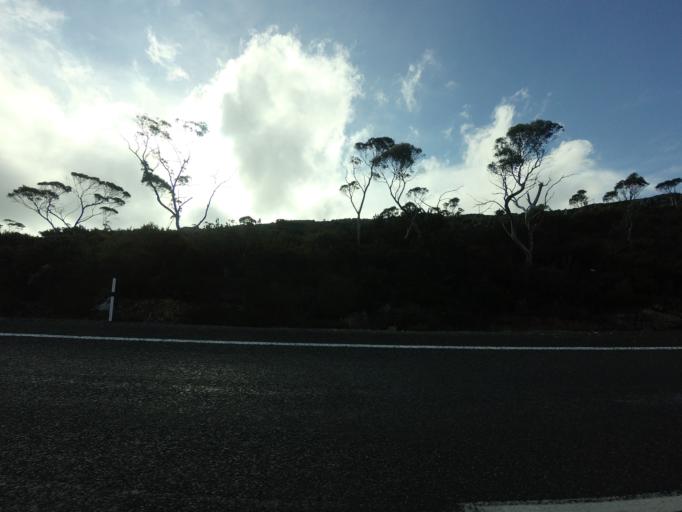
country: AU
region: Tasmania
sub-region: Meander Valley
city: Deloraine
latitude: -41.7301
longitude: 146.7108
